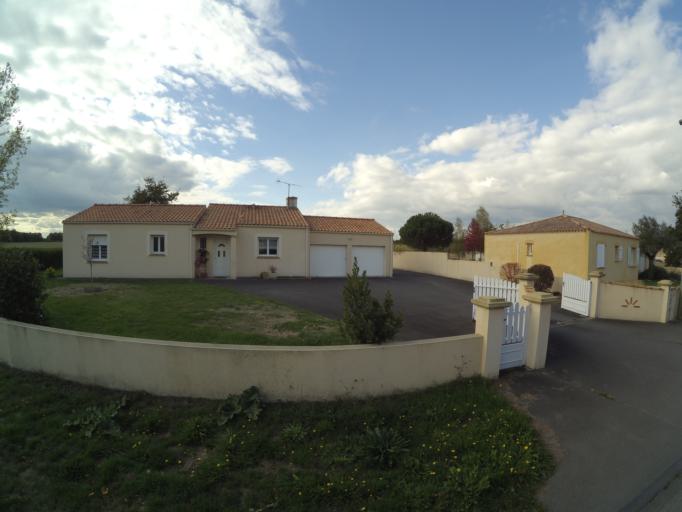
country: FR
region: Pays de la Loire
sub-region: Departement de la Loire-Atlantique
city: Saint-Lumine-de-Clisson
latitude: 47.0816
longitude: -1.3481
